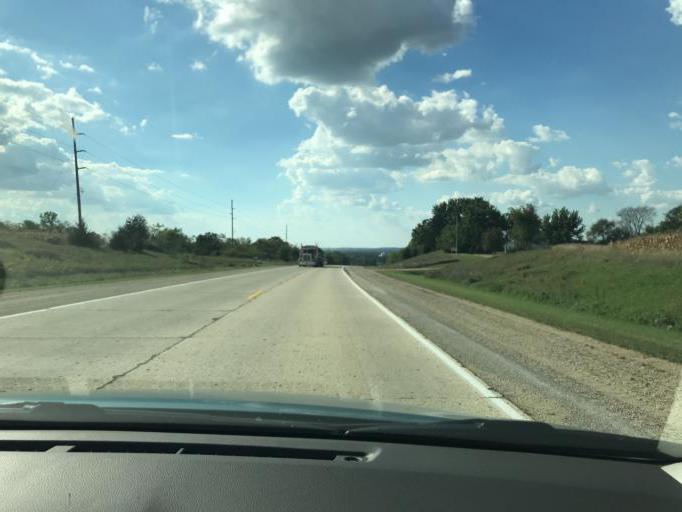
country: US
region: Wisconsin
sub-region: Green County
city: Brodhead
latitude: 42.5606
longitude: -89.3202
